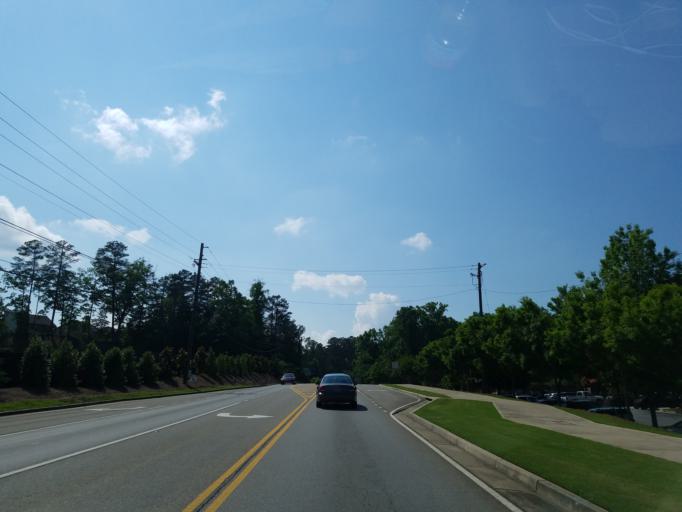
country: US
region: Georgia
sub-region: Cherokee County
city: Holly Springs
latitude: 34.1361
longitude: -84.5002
